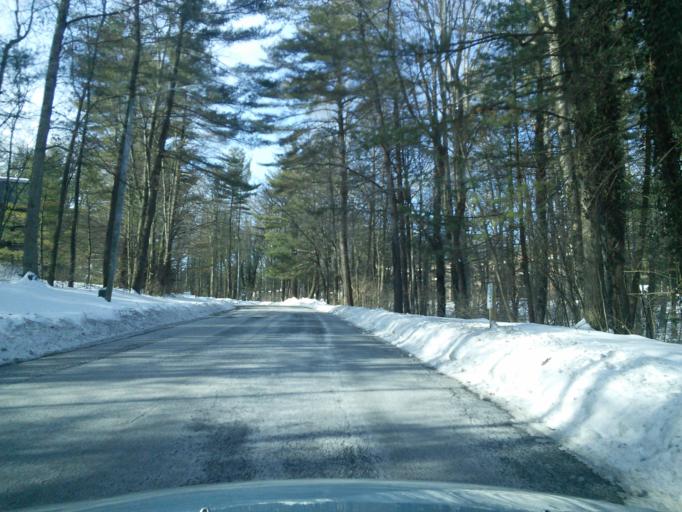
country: US
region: Pennsylvania
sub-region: Centre County
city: Park Forest Village
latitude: 40.8311
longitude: -77.8832
